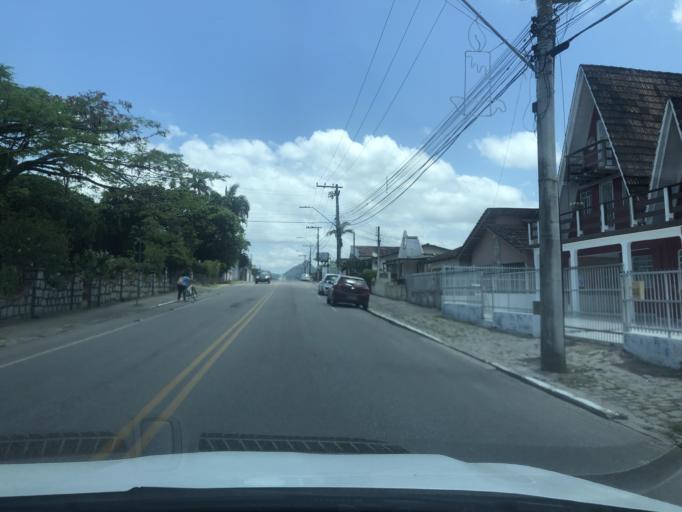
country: BR
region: Santa Catarina
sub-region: Sao Francisco Do Sul
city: Sao Francisco do Sul
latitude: -26.2517
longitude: -48.6417
